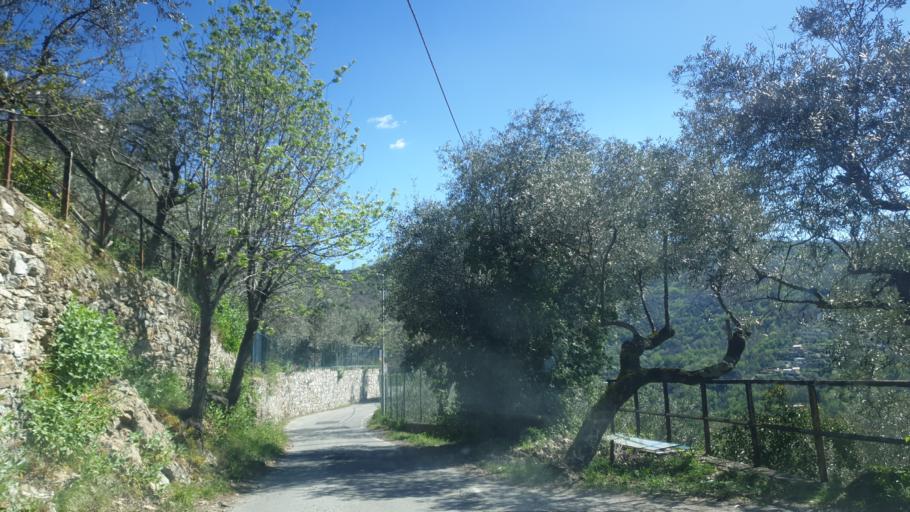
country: IT
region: Liguria
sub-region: Provincia di Genova
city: Recco
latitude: 44.3718
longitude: 9.1446
